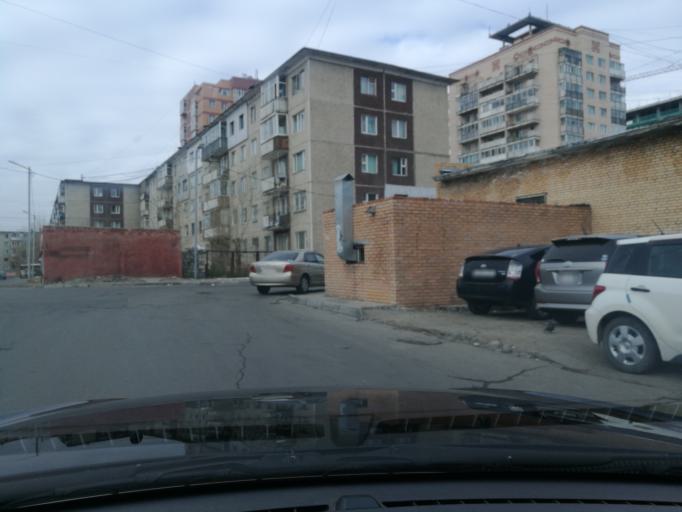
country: MN
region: Ulaanbaatar
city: Ulaanbaatar
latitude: 47.9119
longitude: 106.9024
